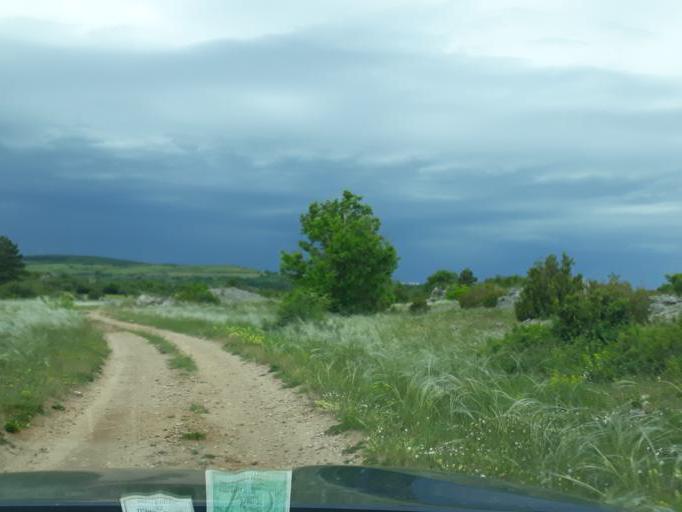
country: FR
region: Languedoc-Roussillon
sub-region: Departement de l'Herault
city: Lodeve
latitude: 43.8163
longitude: 3.2794
